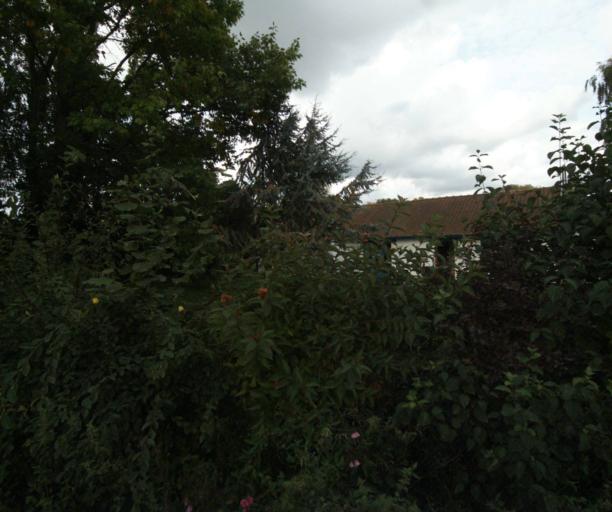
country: FR
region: Nord-Pas-de-Calais
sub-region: Departement du Nord
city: Wavrin
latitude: 50.5649
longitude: 2.9361
